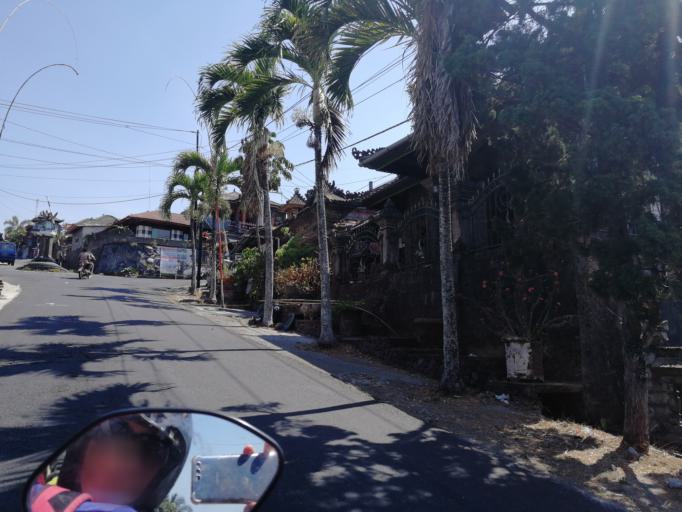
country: ID
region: Bali
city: Banjar Kedisan
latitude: -8.1488
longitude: 115.3063
